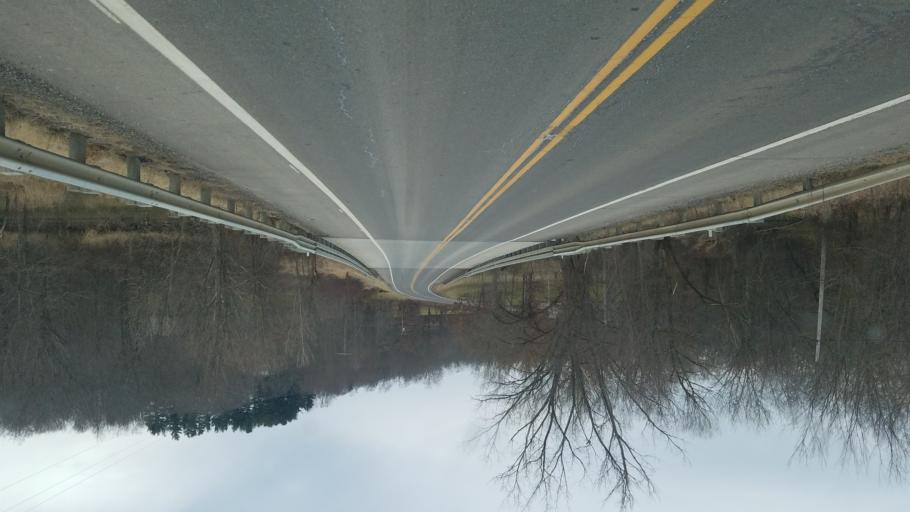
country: US
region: Ohio
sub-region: Richland County
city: Lincoln Heights
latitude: 40.7212
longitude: -82.3728
